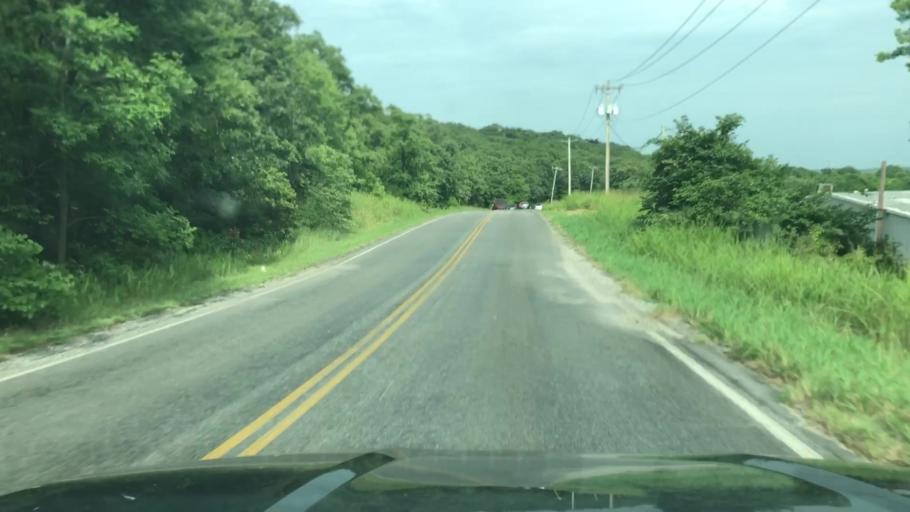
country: US
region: Oklahoma
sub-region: Tulsa County
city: Oakhurst
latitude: 36.0907
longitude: -96.0813
